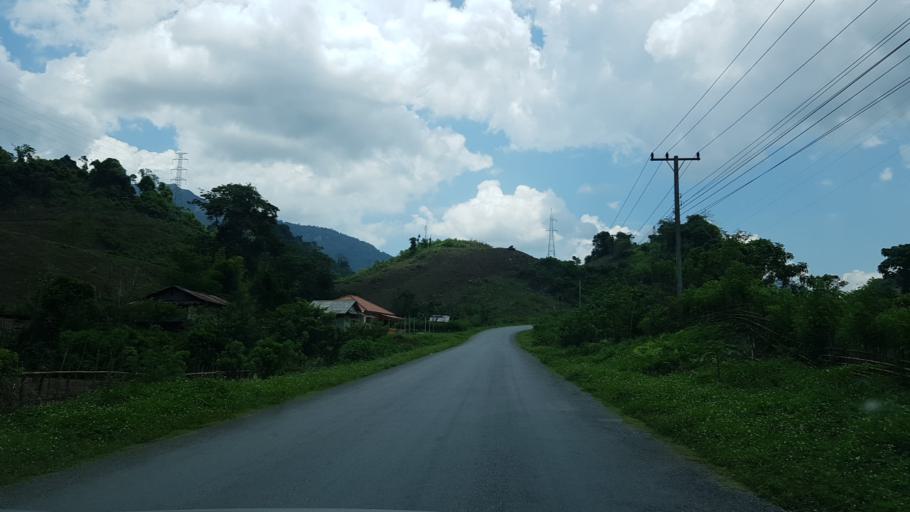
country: LA
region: Vientiane
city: Muang Kasi
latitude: 19.1396
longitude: 102.3024
